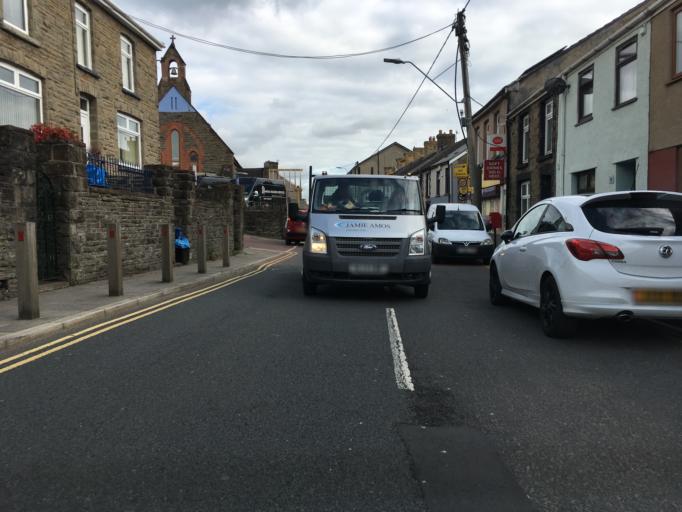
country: GB
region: Wales
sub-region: Merthyr Tydfil County Borough
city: Treharris
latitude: 51.6683
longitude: -3.2975
